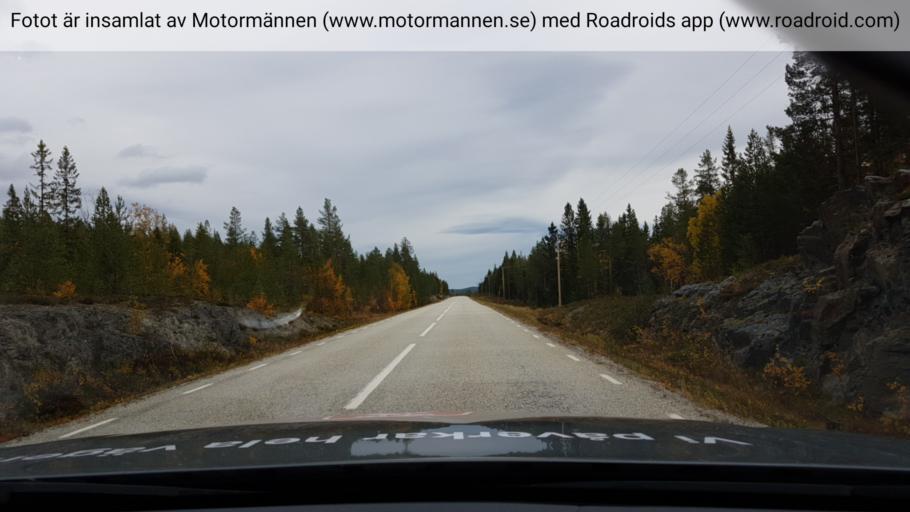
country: SE
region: Jaemtland
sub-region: Are Kommun
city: Jarpen
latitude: 62.7739
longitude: 13.7097
